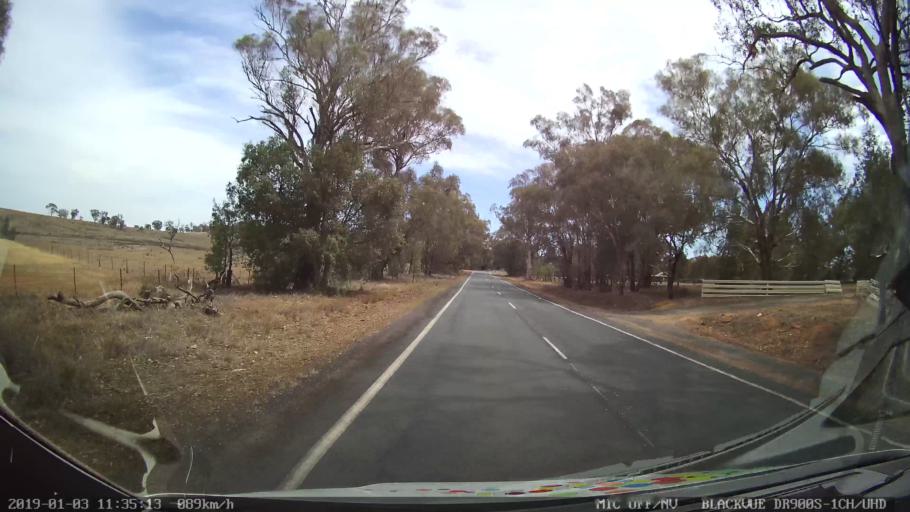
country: AU
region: New South Wales
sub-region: Weddin
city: Grenfell
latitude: -33.9251
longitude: 148.1598
